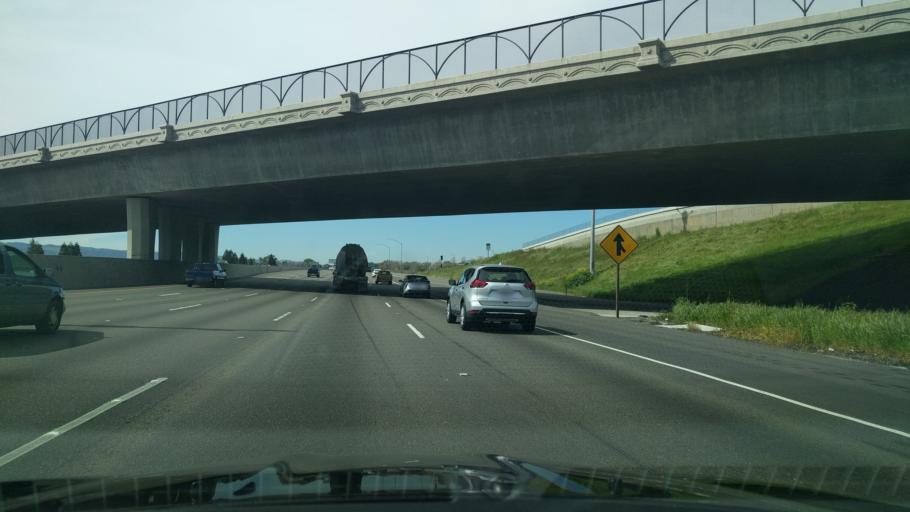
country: US
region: California
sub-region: Alameda County
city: Livermore
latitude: 37.7010
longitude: -121.8011
